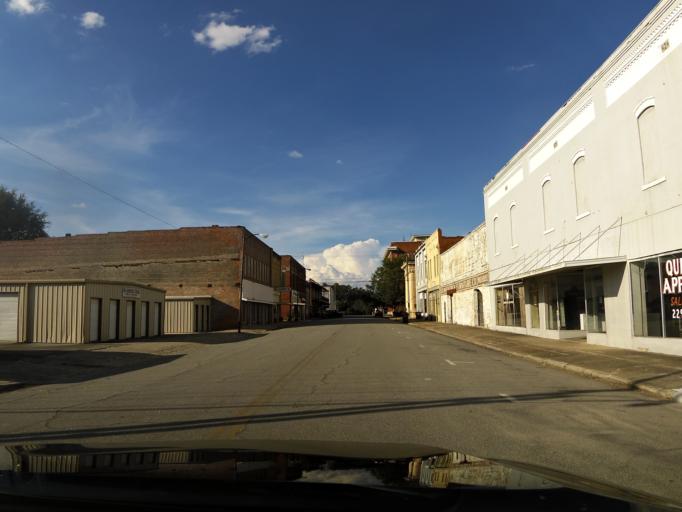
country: US
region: Georgia
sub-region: Brooks County
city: Quitman
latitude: 30.7834
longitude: -83.5583
